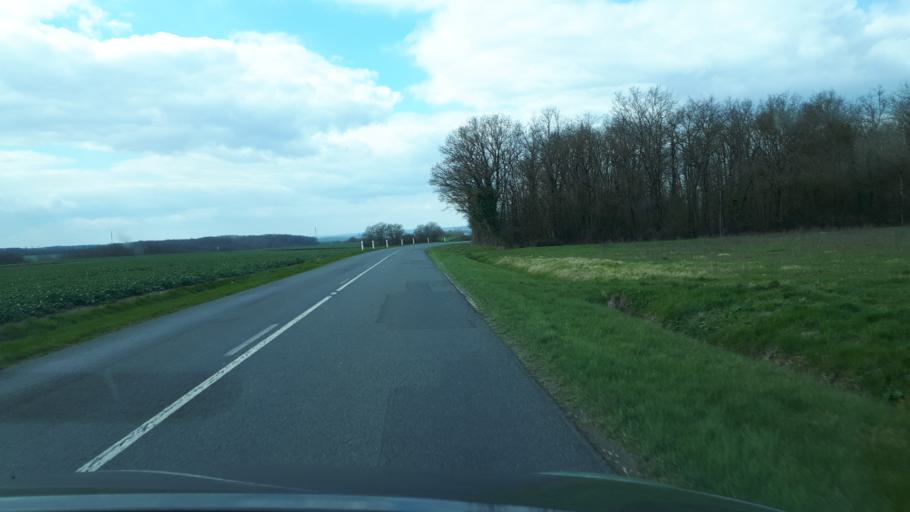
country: FR
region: Centre
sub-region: Departement du Loir-et-Cher
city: Lunay
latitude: 47.7625
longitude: 0.9411
